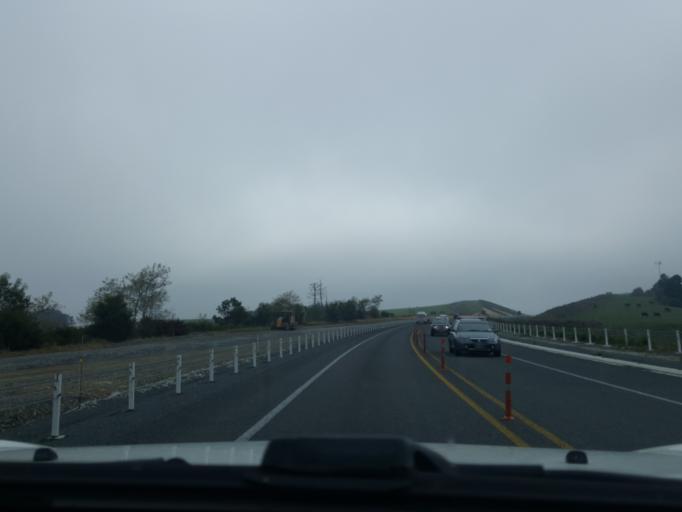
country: NZ
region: Waikato
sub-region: Waikato District
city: Te Kauwhata
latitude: -37.3735
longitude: 175.0948
